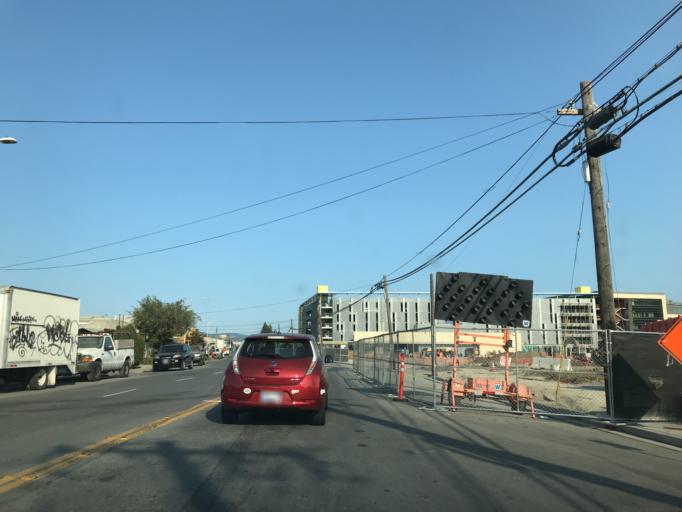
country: US
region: California
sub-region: San Mateo County
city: North Fair Oaks
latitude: 37.4828
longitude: -122.2015
